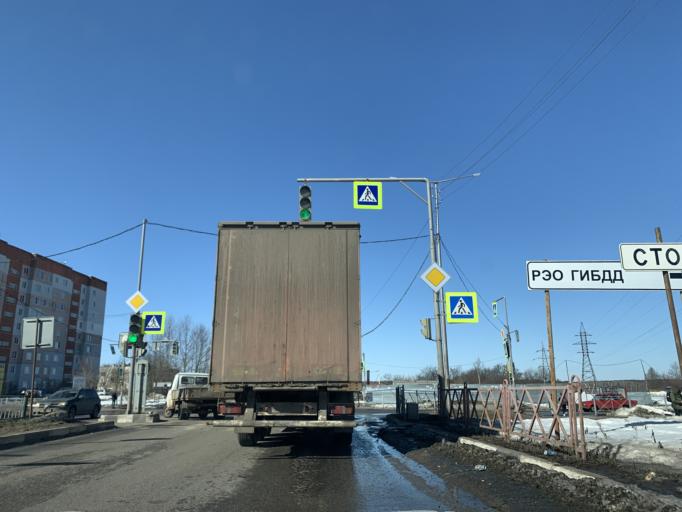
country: RU
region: Jaroslavl
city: Tutayev
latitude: 57.8654
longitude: 39.5085
